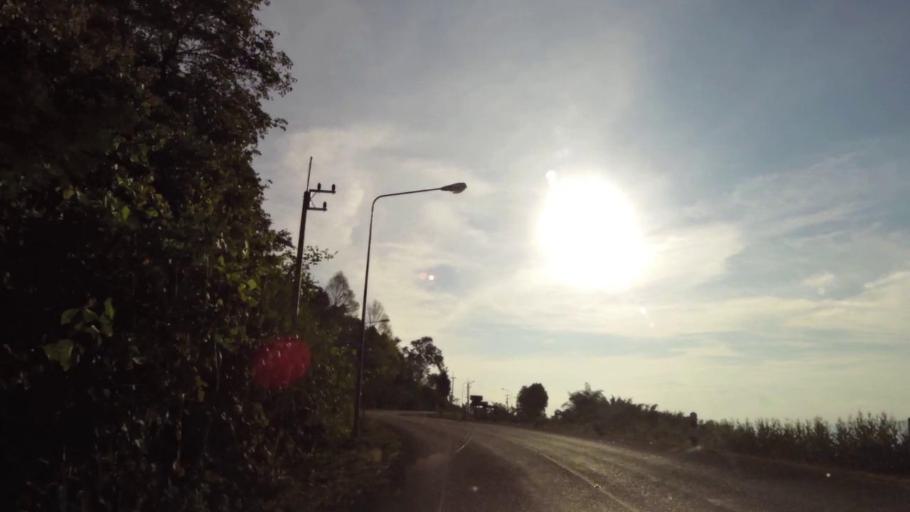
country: TH
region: Chiang Rai
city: Khun Tan
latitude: 19.8592
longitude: 100.4345
